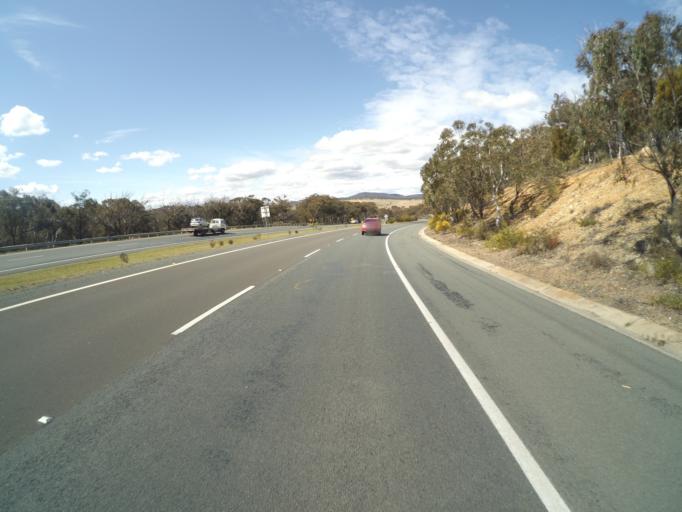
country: AU
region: New South Wales
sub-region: Goulburn Mulwaree
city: Goulburn
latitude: -34.7418
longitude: 149.7621
